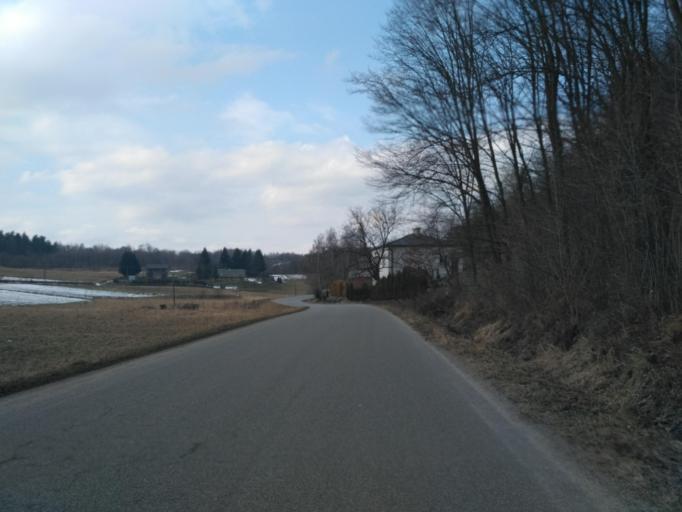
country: PL
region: Subcarpathian Voivodeship
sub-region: Powiat brzozowski
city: Gorki
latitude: 49.6311
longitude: 22.0585
